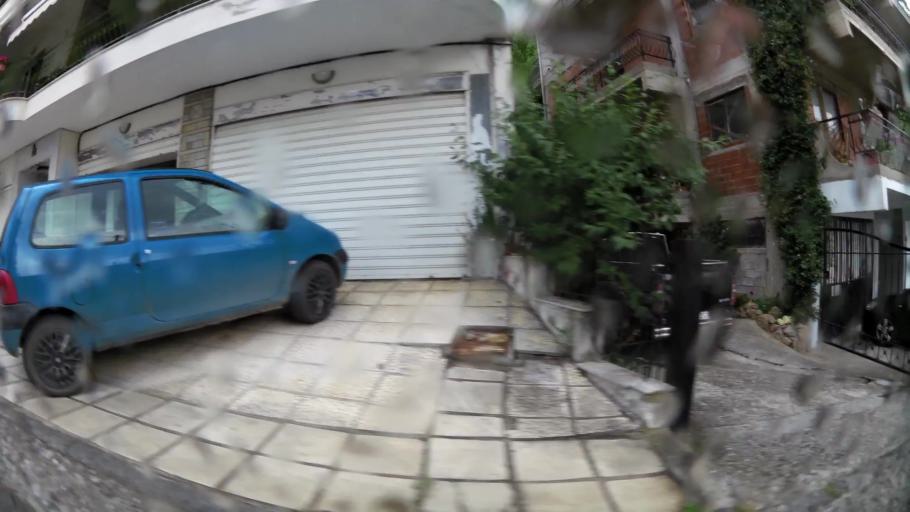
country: GR
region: Central Macedonia
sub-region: Nomos Imathias
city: Veroia
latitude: 40.5242
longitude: 22.1949
